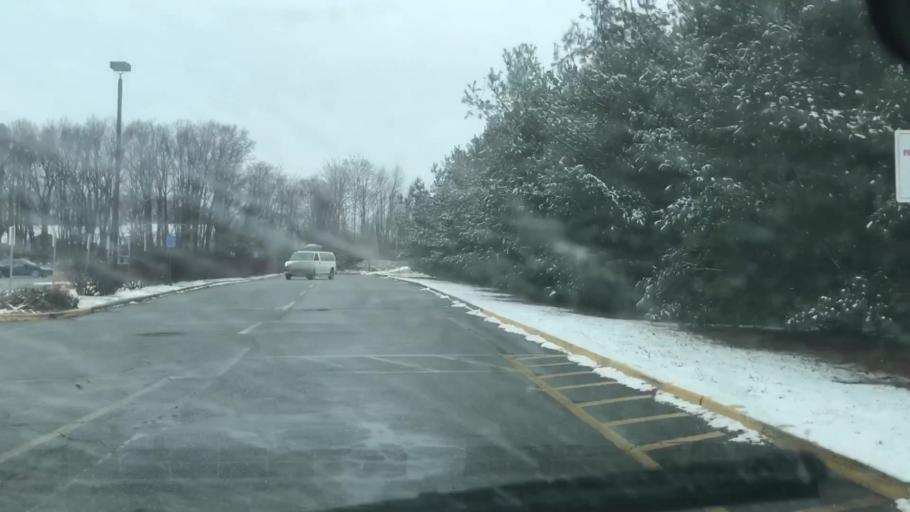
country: US
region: New Jersey
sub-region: Ocean County
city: Lakewood
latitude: 40.0749
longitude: -74.2193
